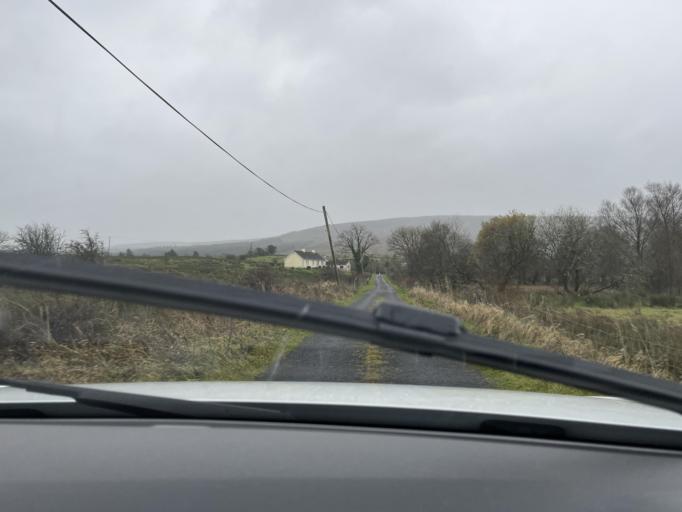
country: IE
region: Connaught
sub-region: County Leitrim
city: Manorhamilton
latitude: 54.2902
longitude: -8.0845
